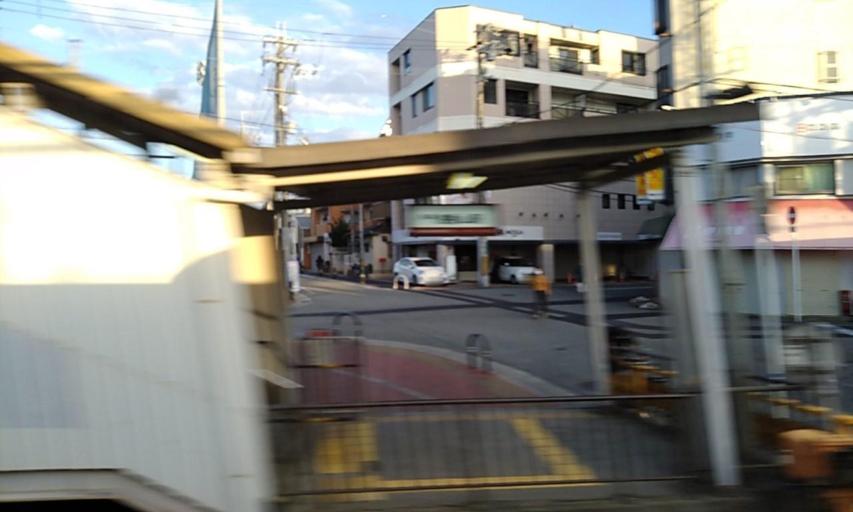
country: JP
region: Osaka
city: Sakai
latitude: 34.5889
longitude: 135.4908
